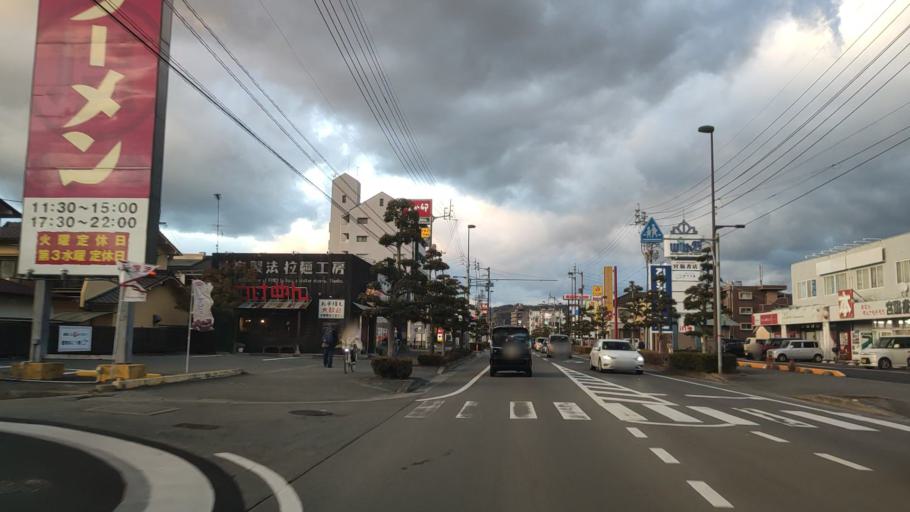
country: JP
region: Ehime
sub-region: Shikoku-chuo Shi
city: Matsuyama
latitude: 33.8337
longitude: 132.7872
